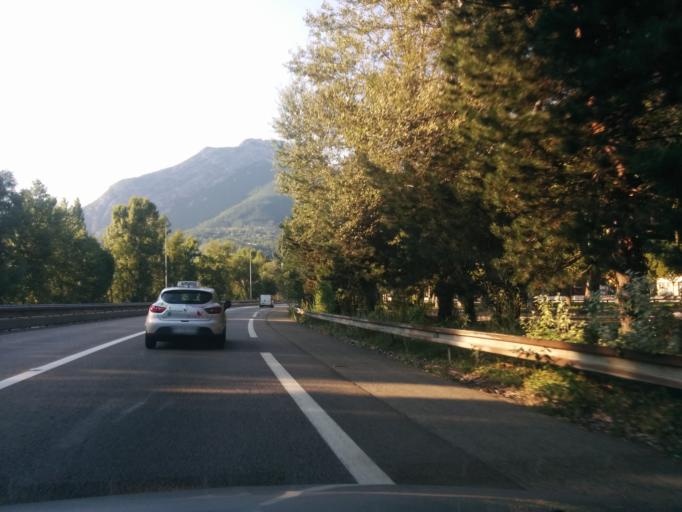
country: FR
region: Rhone-Alpes
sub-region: Departement de l'Isere
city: Saint-Martin-le-Vinoux
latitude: 45.1957
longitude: 5.7162
